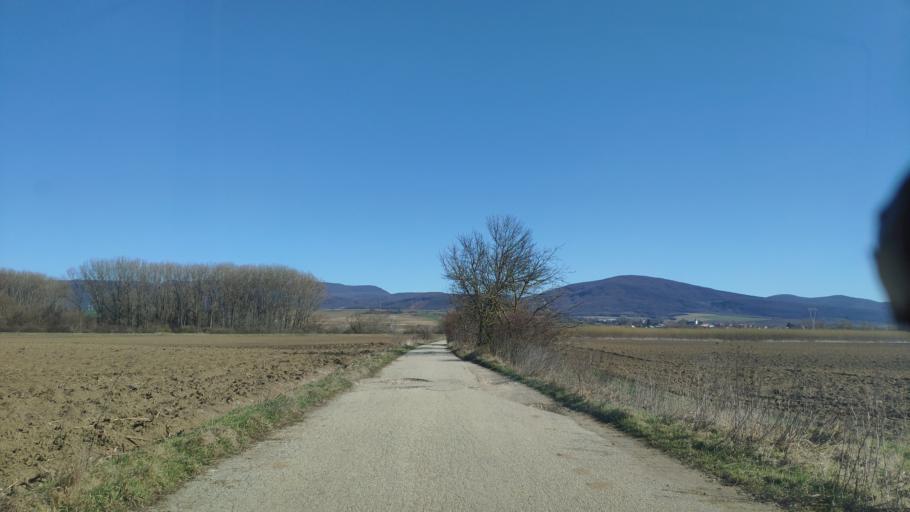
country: HU
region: Borsod-Abauj-Zemplen
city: Gonc
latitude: 48.5888
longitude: 21.3163
